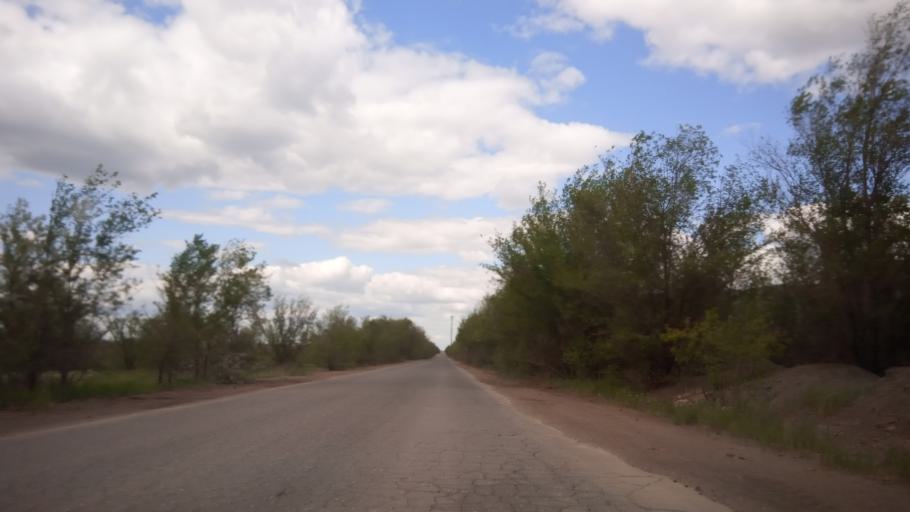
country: RU
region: Orenburg
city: Novotroitsk
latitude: 51.2434
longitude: 58.3575
